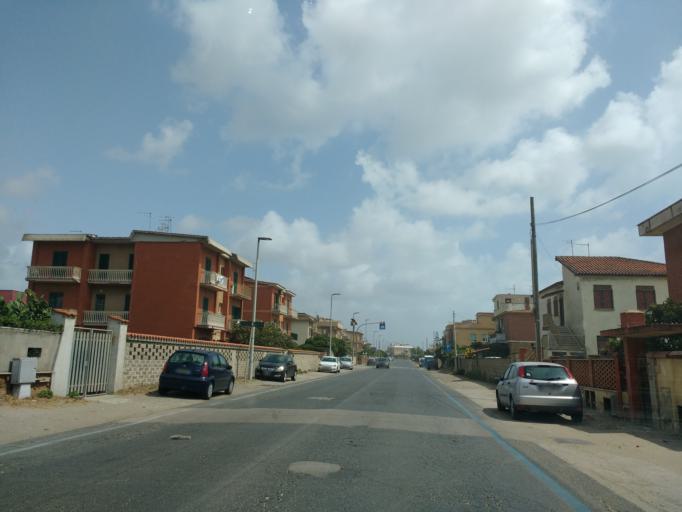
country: IT
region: Latium
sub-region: Citta metropolitana di Roma Capitale
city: Ardea
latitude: 41.6019
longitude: 12.4833
